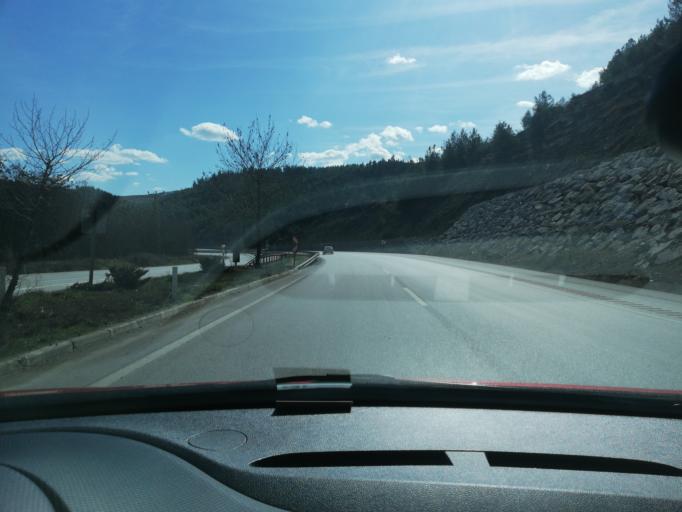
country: TR
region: Karabuk
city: Karabuk
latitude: 41.1633
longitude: 32.6402
